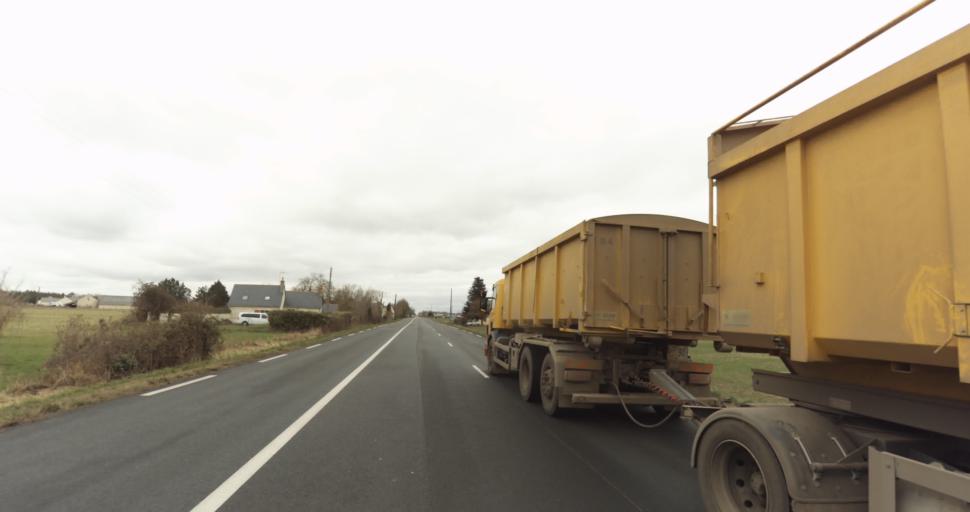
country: FR
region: Pays de la Loire
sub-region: Departement de Maine-et-Loire
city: Vivy
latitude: 47.3114
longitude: -0.0422
